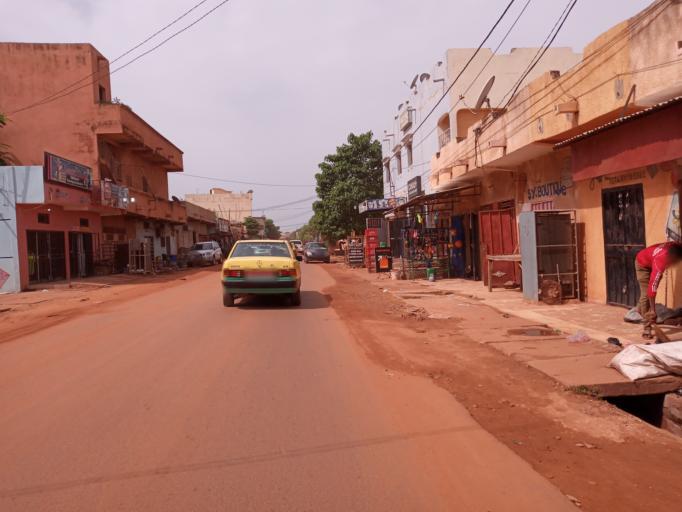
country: ML
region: Bamako
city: Bamako
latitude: 12.5649
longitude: -7.9899
